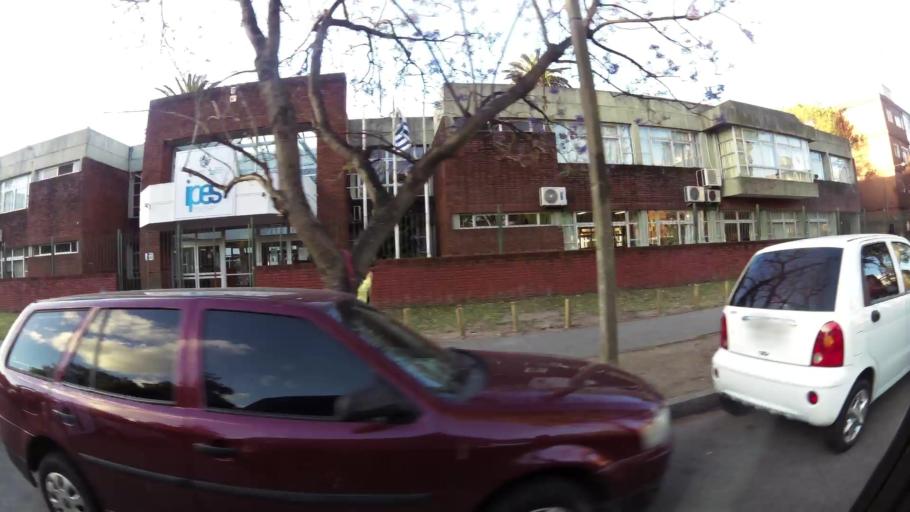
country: UY
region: Montevideo
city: Montevideo
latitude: -34.8821
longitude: -56.1503
